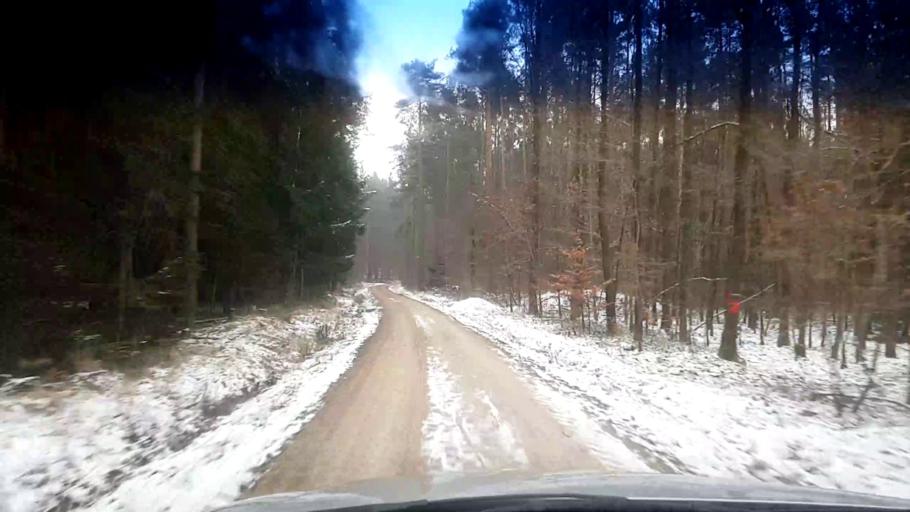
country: DE
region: Bavaria
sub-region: Upper Franconia
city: Gundelsheim
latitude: 49.9638
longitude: 10.9162
